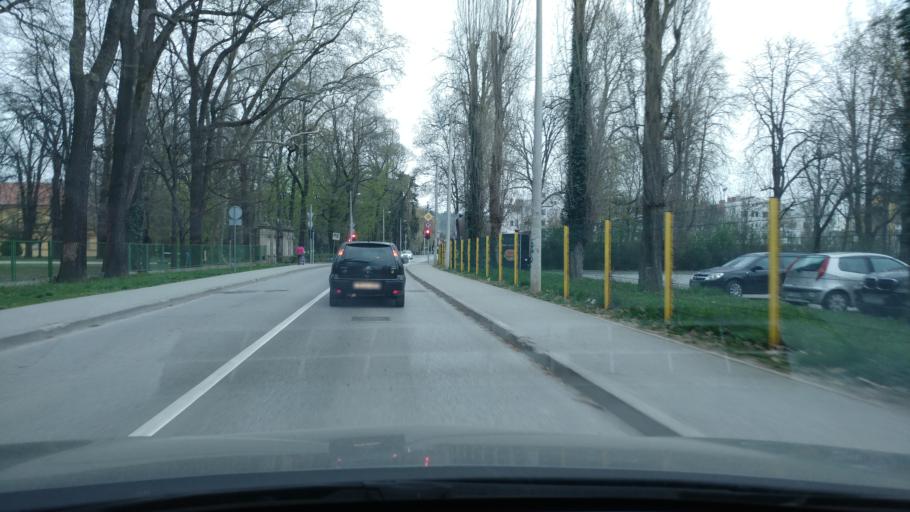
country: HR
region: Grad Zagreb
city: Stenjevec
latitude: 45.8150
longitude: 15.8964
